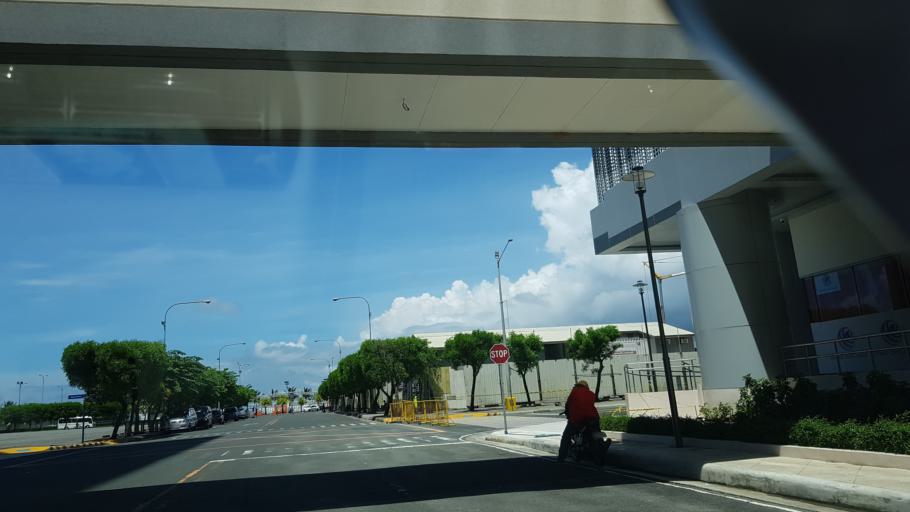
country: PH
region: Metro Manila
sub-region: City of Manila
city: Port Area
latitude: 14.5400
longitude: 120.9811
